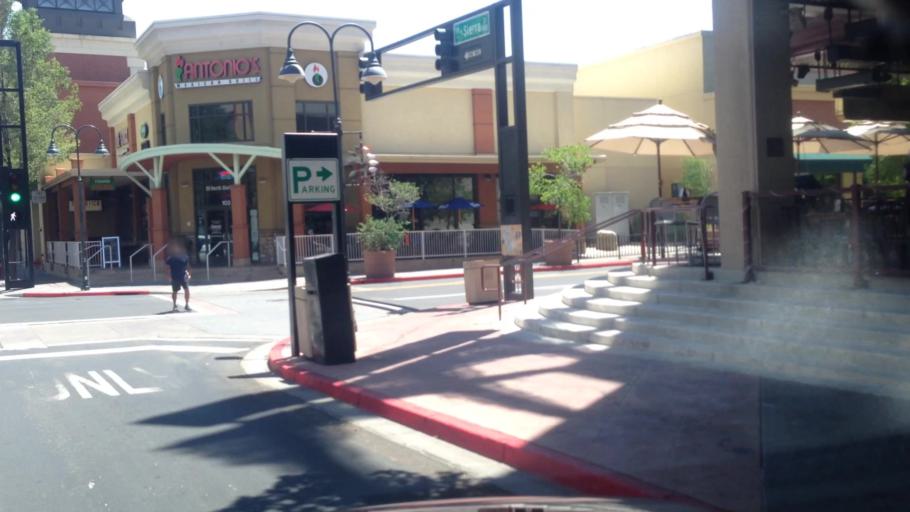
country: US
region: Nevada
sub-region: Washoe County
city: Reno
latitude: 39.5257
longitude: -119.8144
